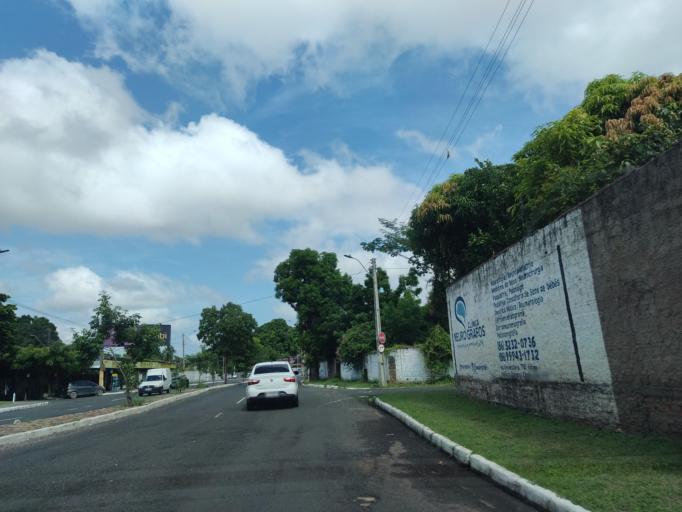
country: BR
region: Piaui
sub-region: Teresina
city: Teresina
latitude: -5.0697
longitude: -42.7974
